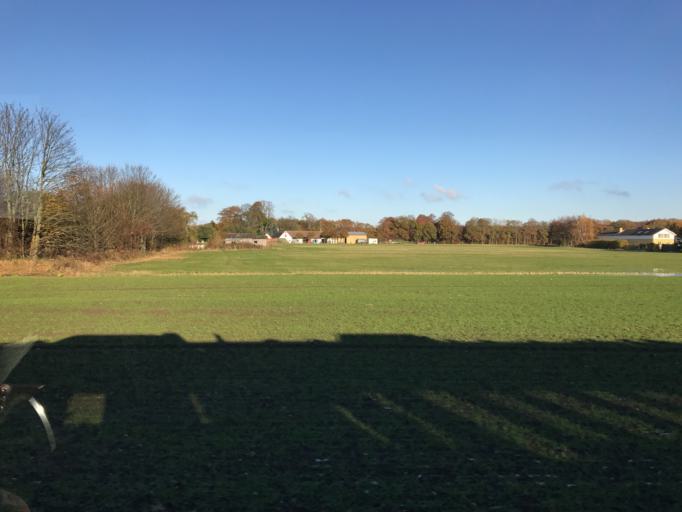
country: DK
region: Zealand
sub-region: Stevns Kommune
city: Store Heddinge
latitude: 55.3406
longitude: 12.3362
